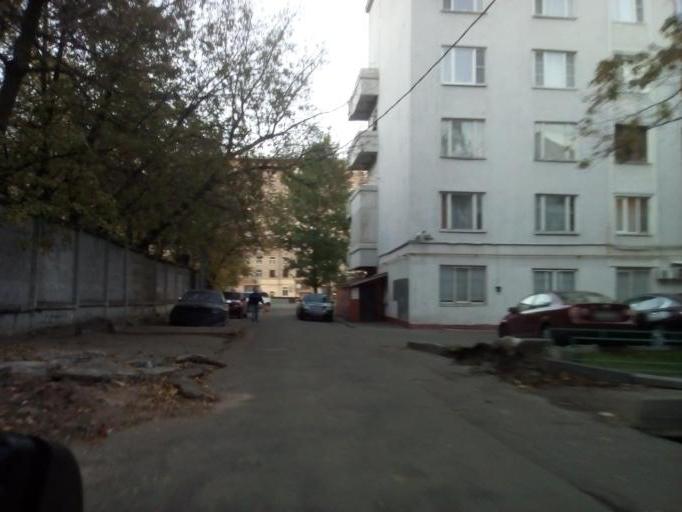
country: RU
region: Moscow
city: Sokol
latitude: 55.8070
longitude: 37.4996
